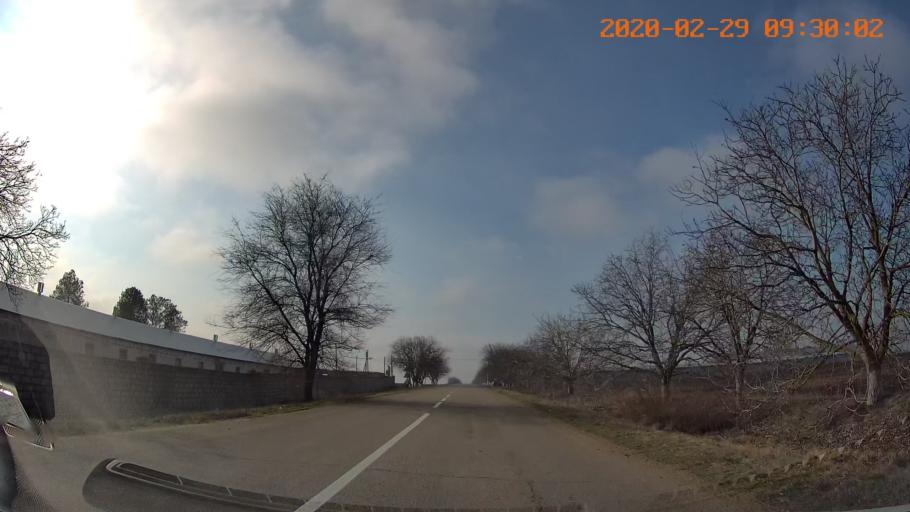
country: UA
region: Odessa
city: Lymanske
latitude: 46.6713
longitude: 29.9184
